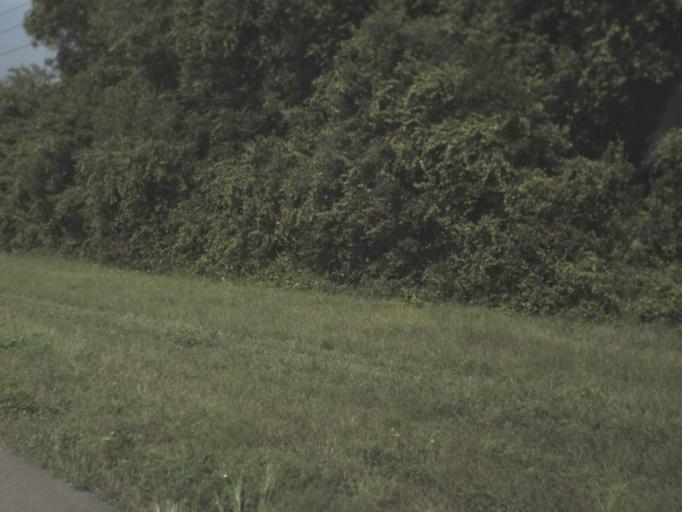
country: US
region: Florida
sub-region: Pasco County
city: Shady Hills
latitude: 28.3616
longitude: -82.5026
